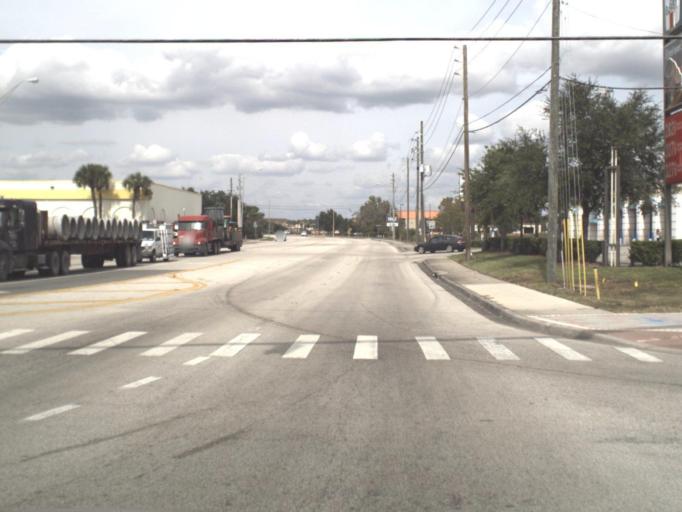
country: US
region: Florida
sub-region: Osceola County
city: Celebration
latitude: 28.3330
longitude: -81.4895
